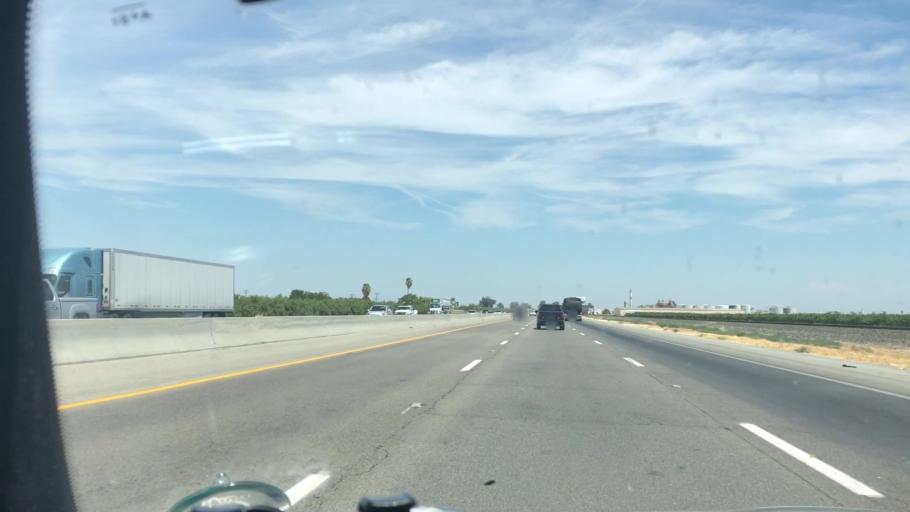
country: US
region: California
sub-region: Kern County
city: McFarland
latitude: 35.7048
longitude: -119.2333
